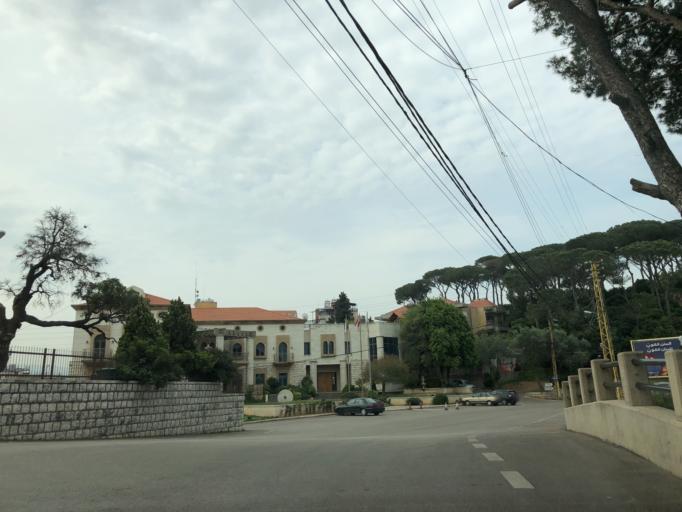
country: LB
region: Mont-Liban
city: Jdaidet el Matn
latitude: 33.8581
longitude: 35.6008
